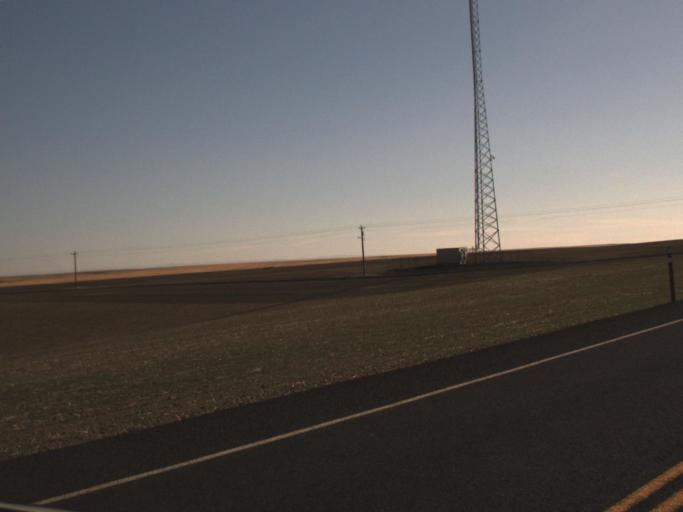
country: US
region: Washington
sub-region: Adams County
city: Ritzville
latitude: 46.9422
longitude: -118.5665
